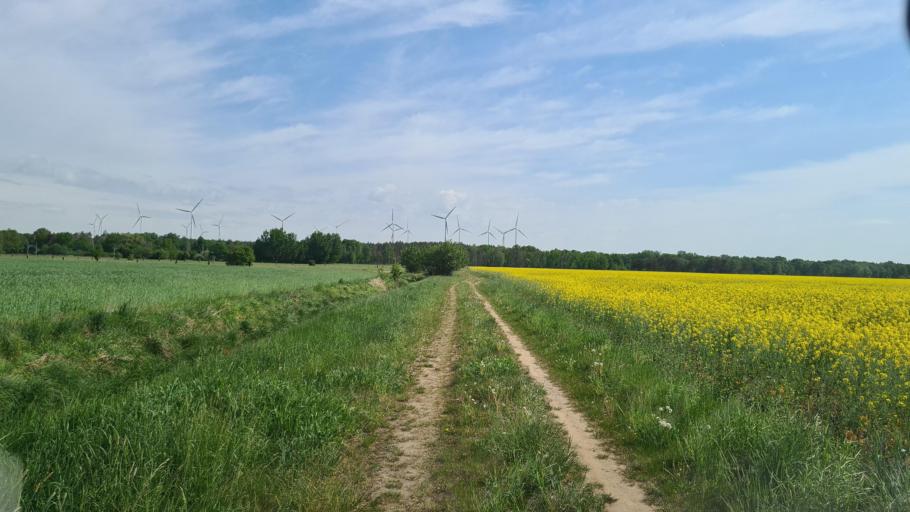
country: DE
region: Brandenburg
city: Falkenberg
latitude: 51.5549
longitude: 13.2840
